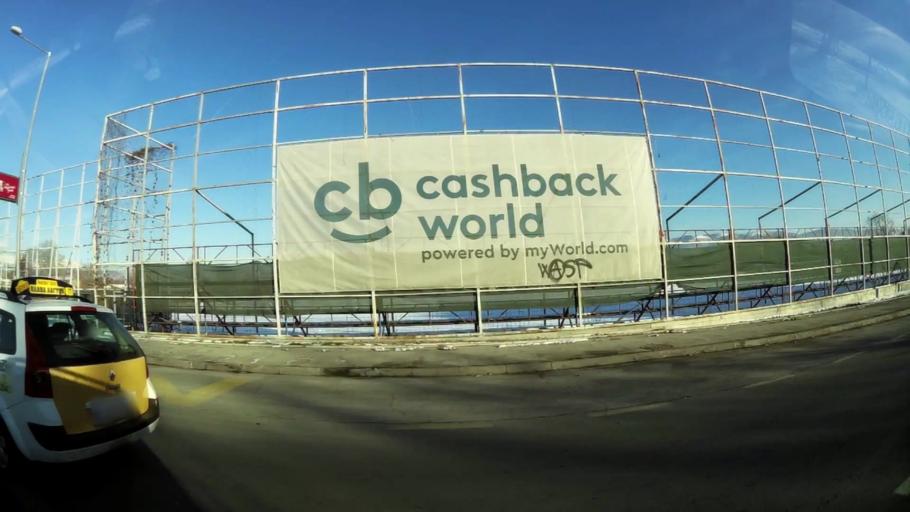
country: MK
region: Karpos
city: Skopje
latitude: 42.0075
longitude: 21.3981
